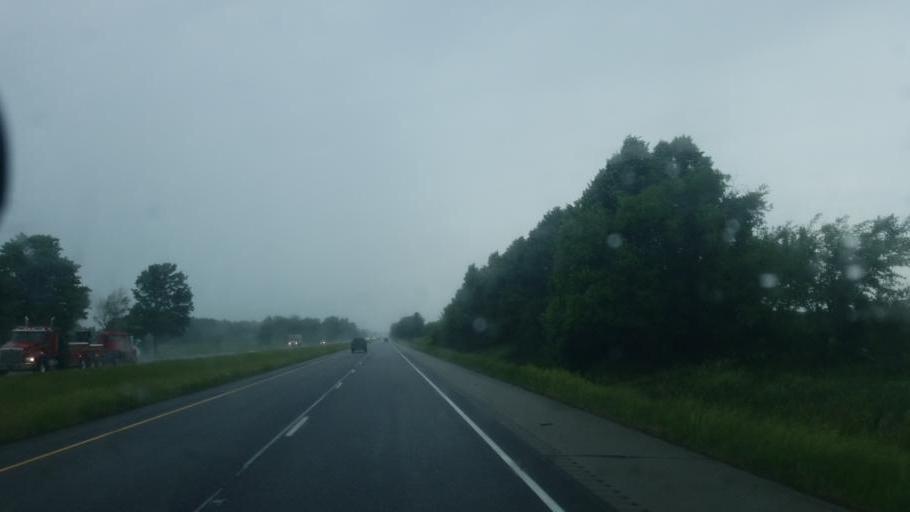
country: US
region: Indiana
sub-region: Whitley County
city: Columbia City
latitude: 41.1331
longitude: -85.4032
